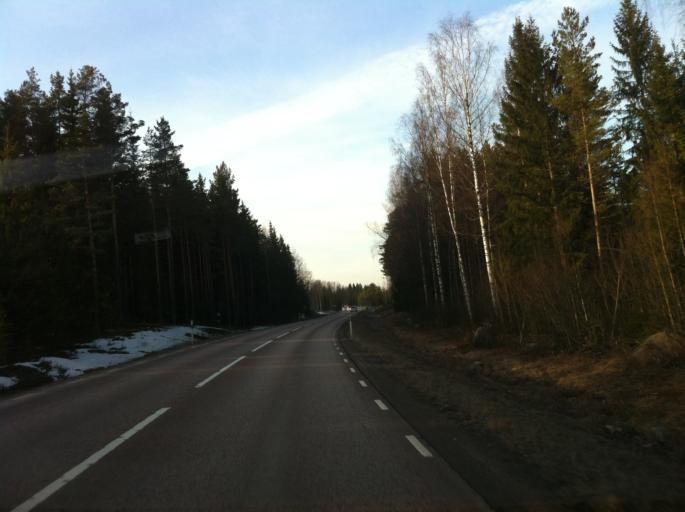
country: SE
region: Vaermland
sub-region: Filipstads Kommun
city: Lesjofors
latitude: 59.9432
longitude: 14.2169
